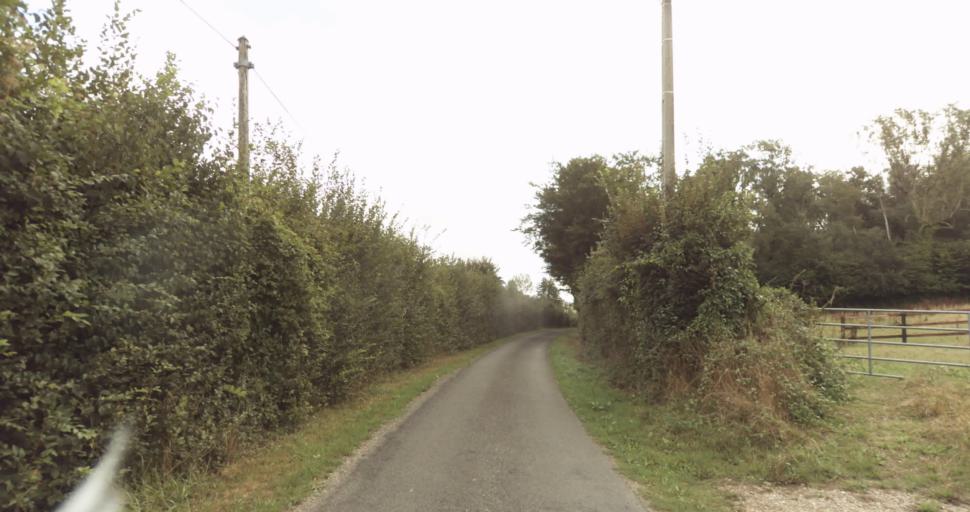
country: FR
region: Lower Normandy
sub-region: Departement de l'Orne
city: Gace
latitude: 48.8449
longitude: 0.2906
